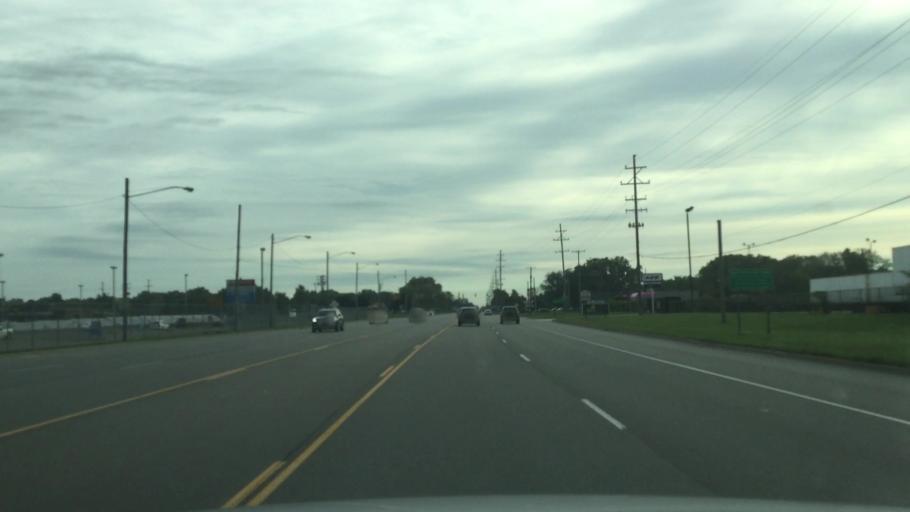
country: US
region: Michigan
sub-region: Genesee County
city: Flint
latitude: 42.9736
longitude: -83.7162
